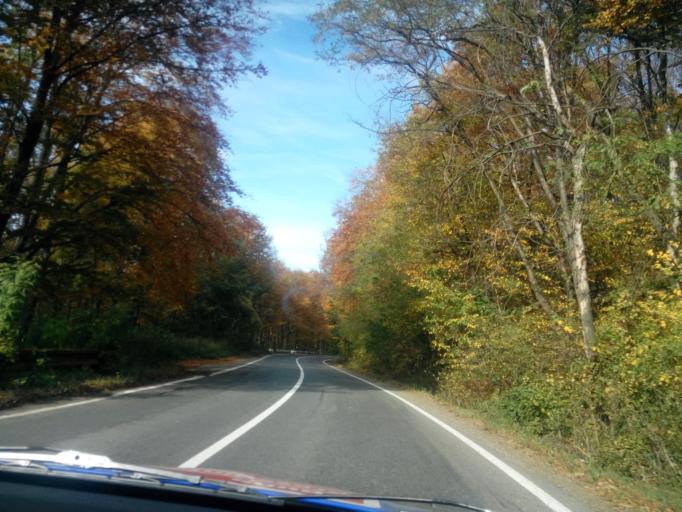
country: RO
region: Bacau
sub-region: Comuna Luizi-Calugara
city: Luizi-Calugara
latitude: 46.5128
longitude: 26.8208
